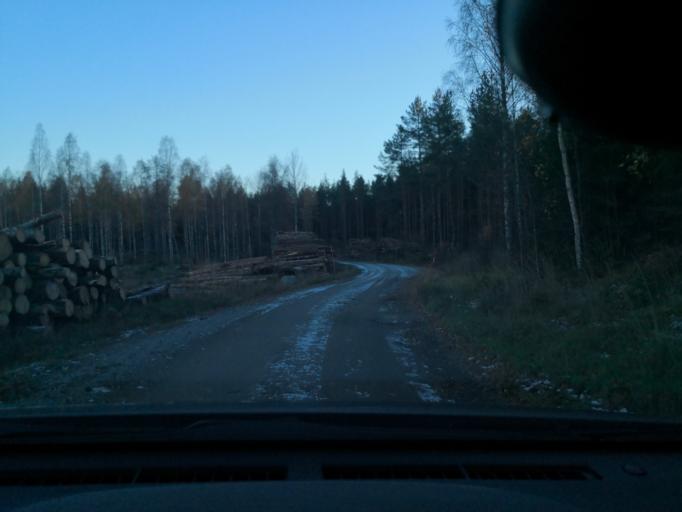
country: SE
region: Vaestmanland
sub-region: Vasteras
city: Tillberga
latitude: 59.7656
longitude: 16.6113
